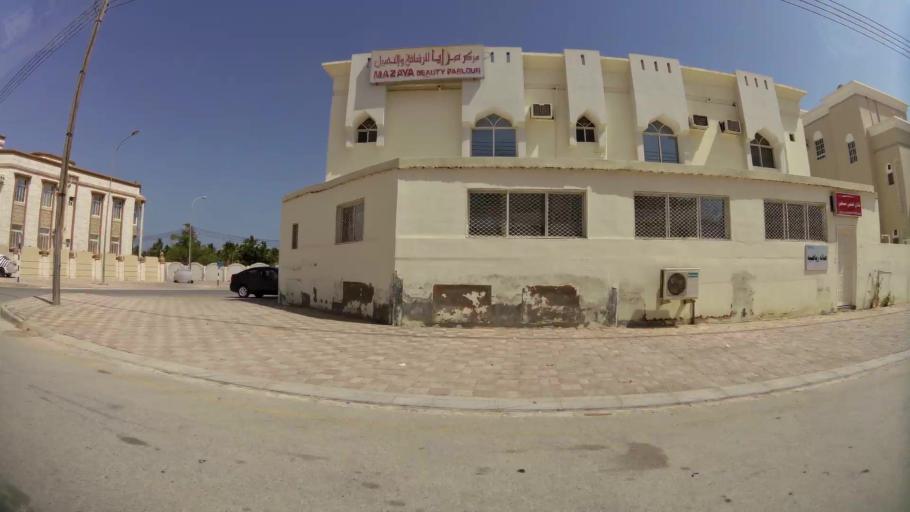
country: OM
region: Zufar
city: Salalah
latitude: 17.0182
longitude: 54.0696
